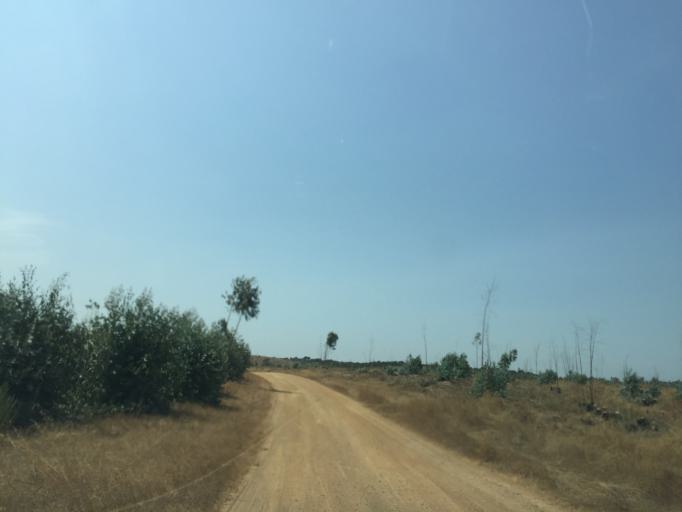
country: PT
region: Setubal
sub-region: Grandola
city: Grandola
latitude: 38.0481
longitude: -8.4635
